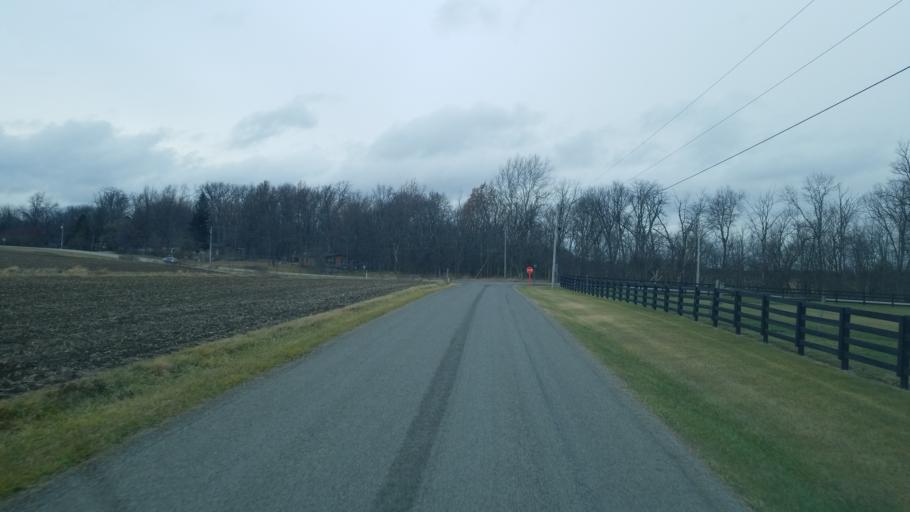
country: US
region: Ohio
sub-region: Union County
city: Richwood
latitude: 40.3384
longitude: -83.2496
